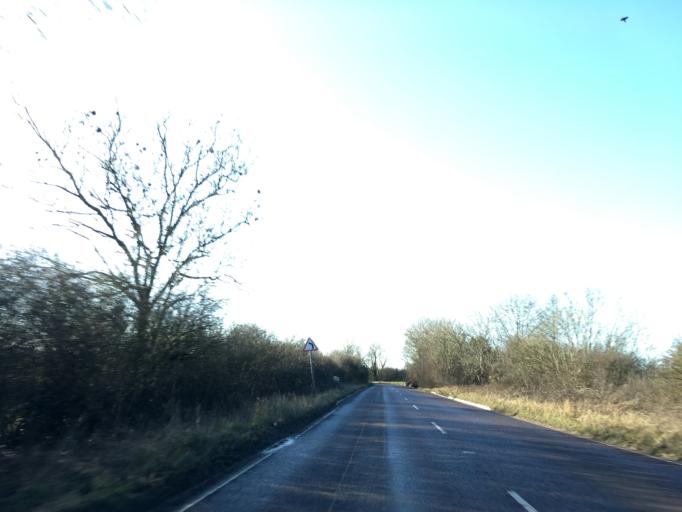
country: GB
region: England
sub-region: Wiltshire
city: Minety
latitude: 51.6188
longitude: -1.9445
